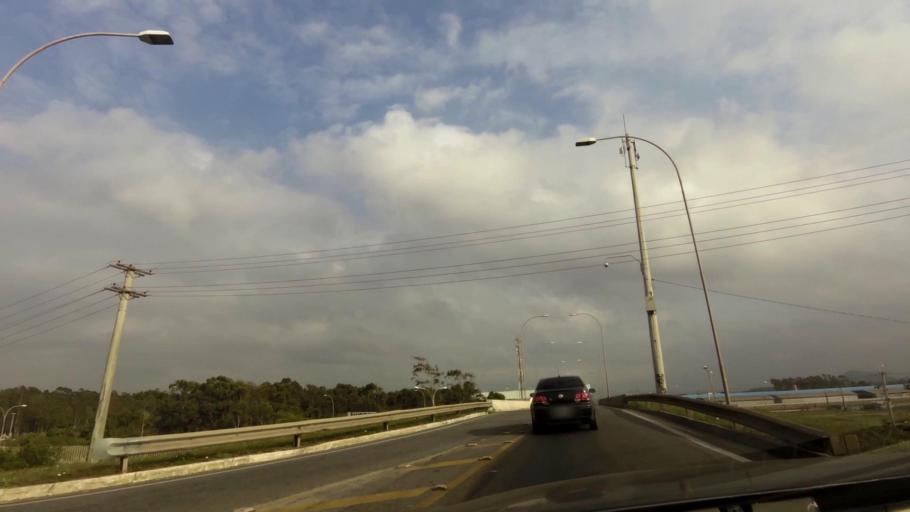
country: BR
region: Espirito Santo
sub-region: Vila Velha
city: Vila Velha
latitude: -20.3952
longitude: -40.3187
